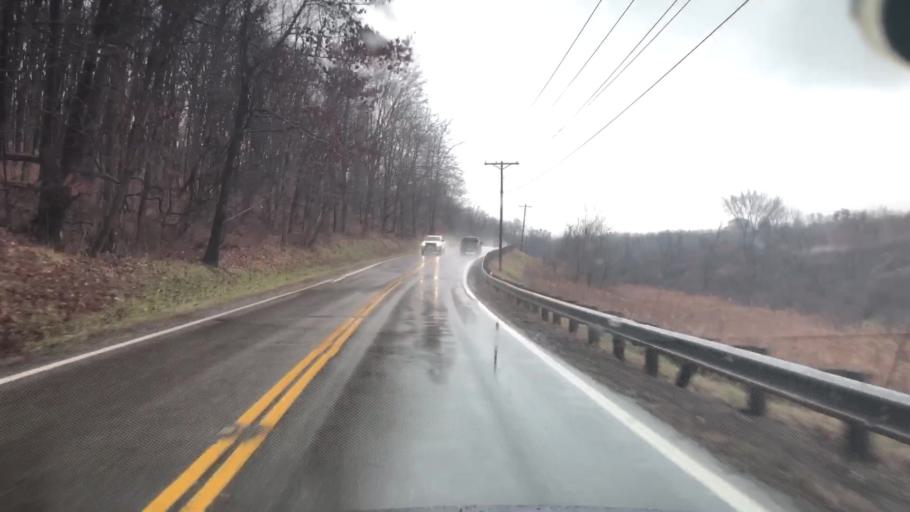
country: US
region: Ohio
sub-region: Belmont County
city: Saint Clairsville
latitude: 40.1602
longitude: -80.9784
